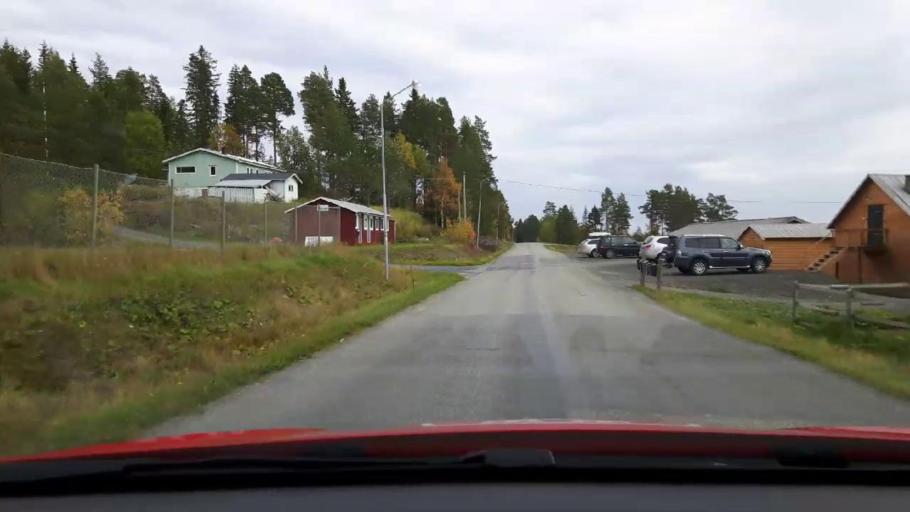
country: SE
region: Jaemtland
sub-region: Krokoms Kommun
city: Valla
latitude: 63.2586
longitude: 14.0149
